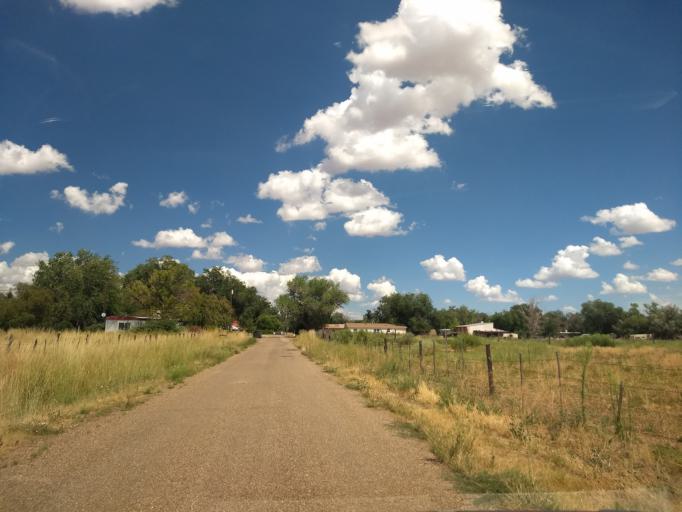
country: US
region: Arizona
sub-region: Coconino County
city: Fredonia
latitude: 36.9440
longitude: -112.5308
